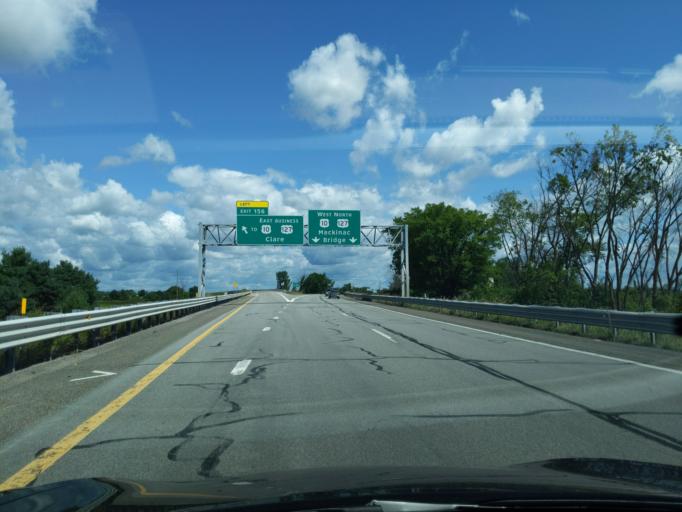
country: US
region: Michigan
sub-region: Clare County
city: Clare
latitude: 43.7978
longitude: -84.7585
